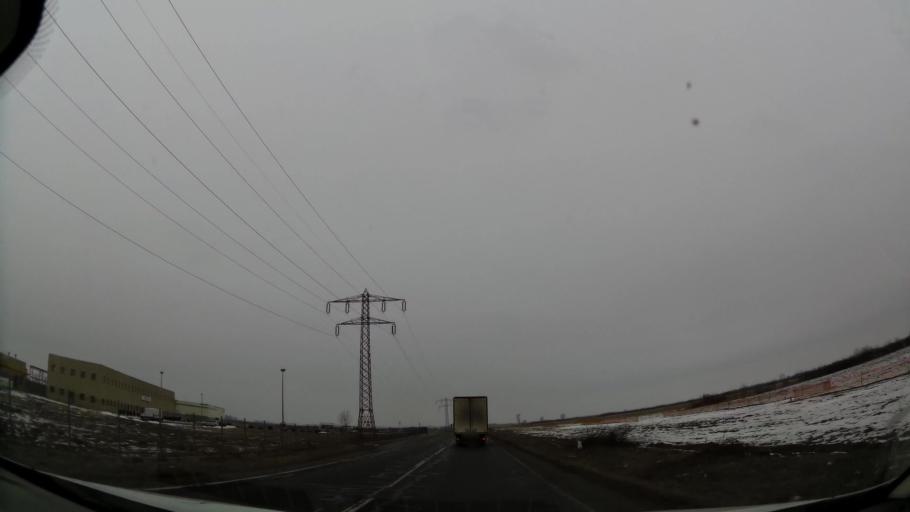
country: RO
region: Dambovita
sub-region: Comuna Contesti
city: Balteni
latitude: 44.6525
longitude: 25.6886
